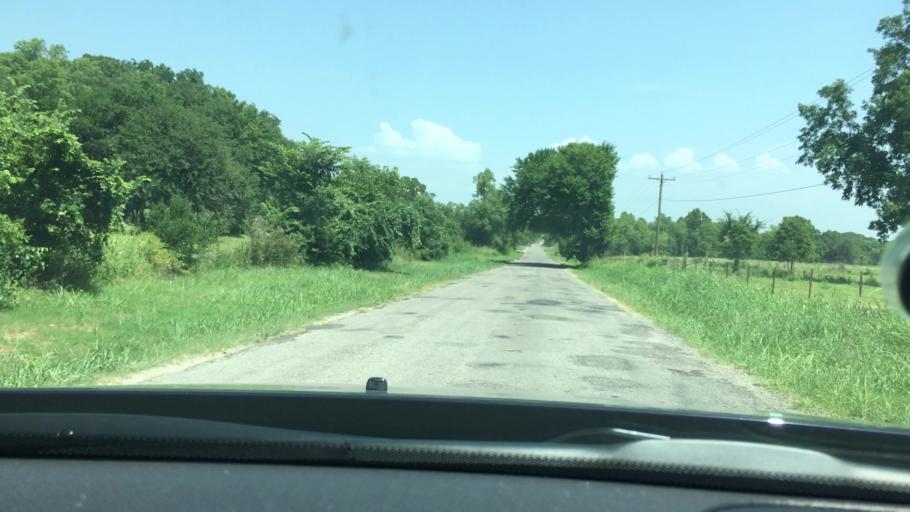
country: US
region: Oklahoma
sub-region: Pontotoc County
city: Byng
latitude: 34.8337
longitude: -96.6698
